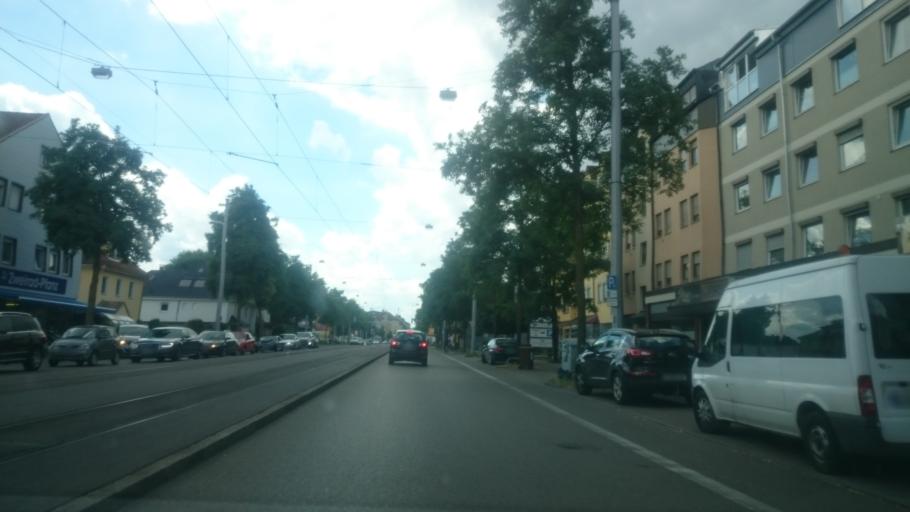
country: DE
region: Bavaria
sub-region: Swabia
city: Augsburg
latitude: 48.3915
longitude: 10.8815
